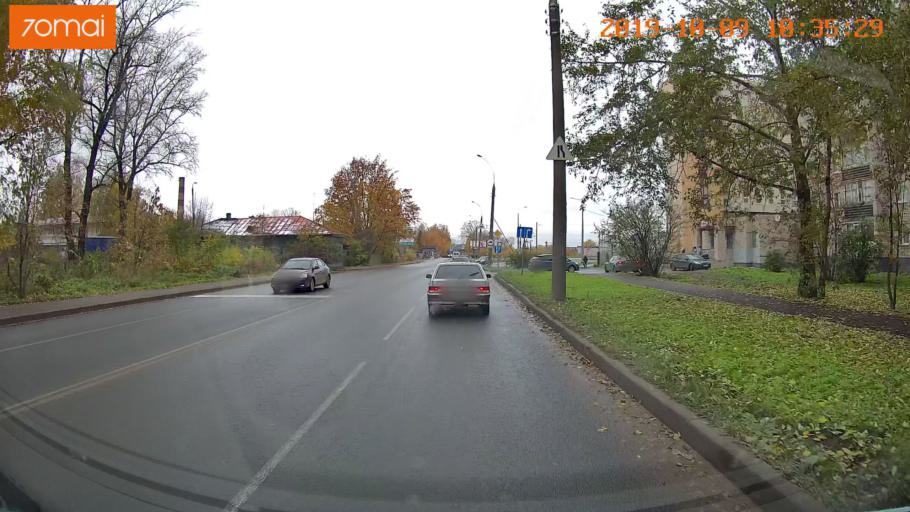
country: RU
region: Vologda
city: Vologda
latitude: 59.2267
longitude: 39.8631
